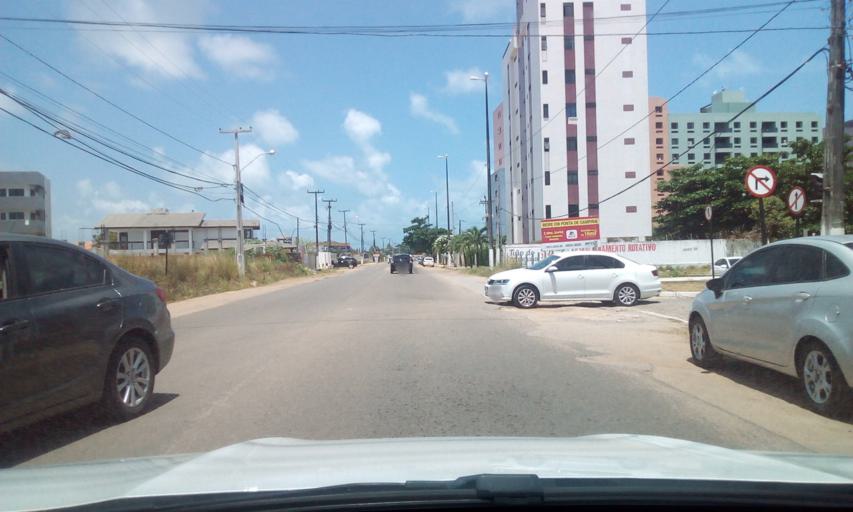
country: BR
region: Paraiba
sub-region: Cabedelo
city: Cabedelo
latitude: -7.0308
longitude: -34.8336
